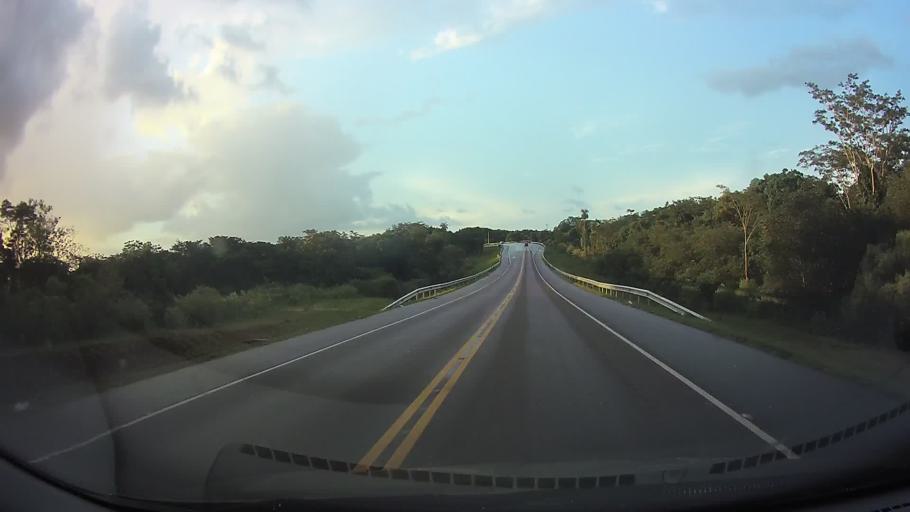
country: PY
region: Paraguari
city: Paraguari
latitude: -25.6065
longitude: -57.1861
